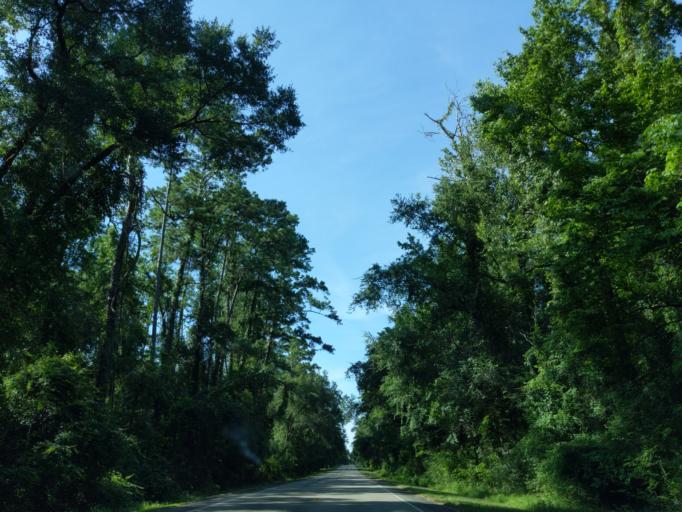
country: US
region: Florida
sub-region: Leon County
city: Woodville
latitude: 30.2485
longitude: -84.3130
